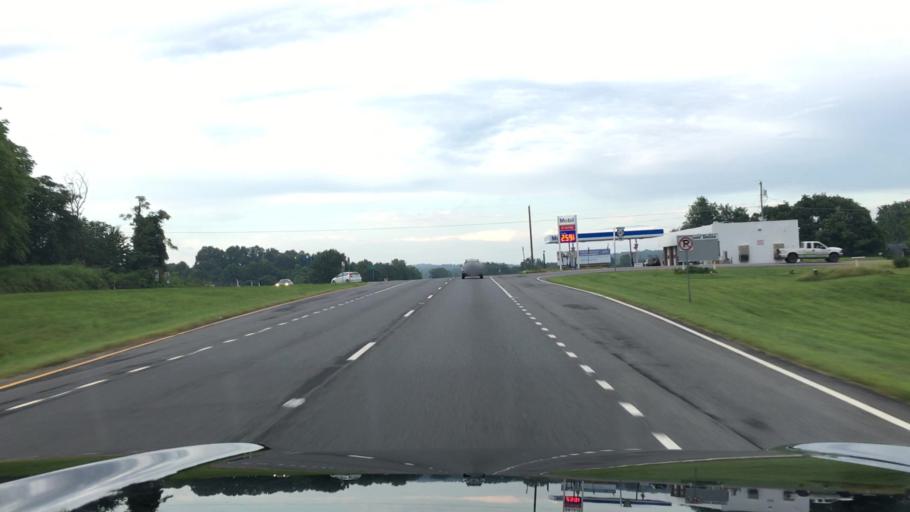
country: US
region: Virginia
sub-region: Madison County
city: Madison
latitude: 38.3204
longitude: -78.3089
